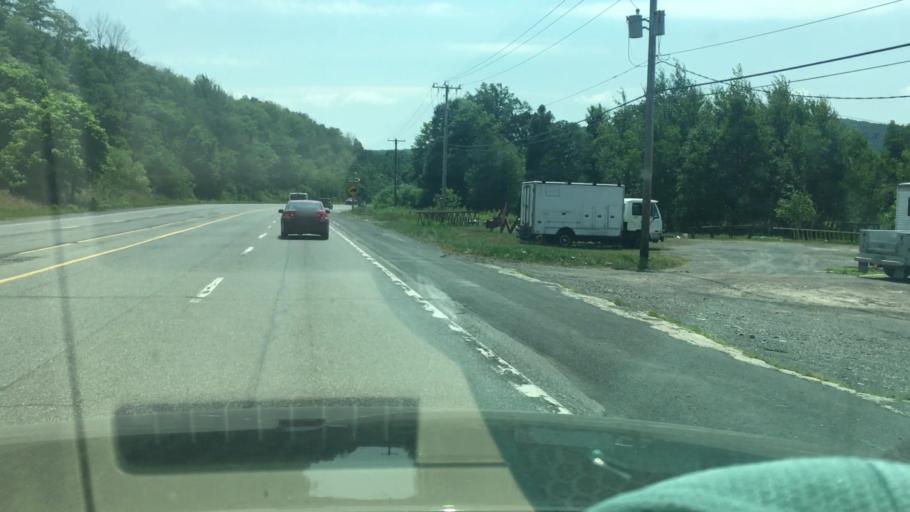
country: US
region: Pennsylvania
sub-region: Schuylkill County
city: Tamaqua
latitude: 40.7634
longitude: -75.9527
